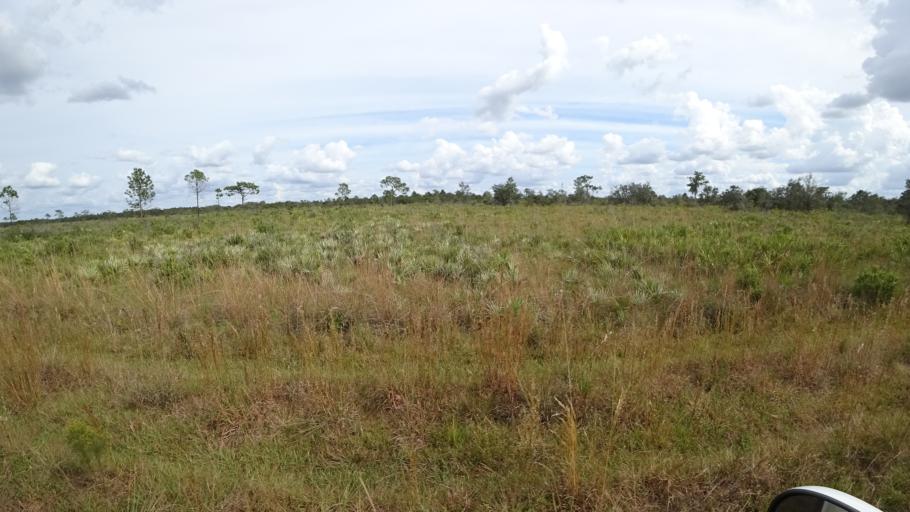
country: US
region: Florida
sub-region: Hillsborough County
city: Wimauma
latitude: 27.5599
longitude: -82.1430
